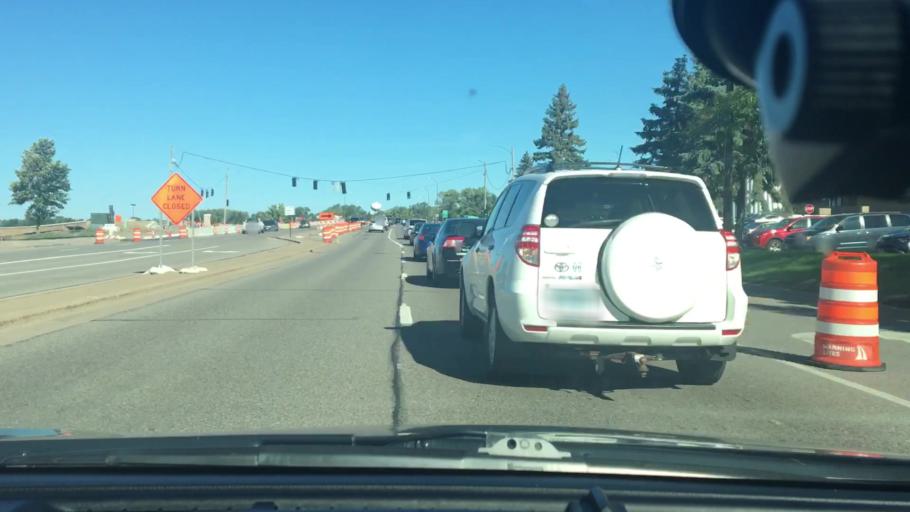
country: US
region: Minnesota
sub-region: Hennepin County
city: Minnetonka Mills
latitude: 44.9682
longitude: -93.4432
